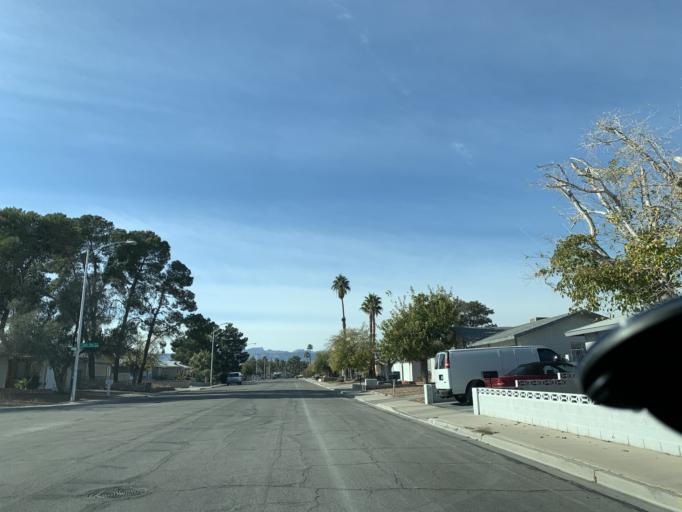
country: US
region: Nevada
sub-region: Clark County
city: Spring Valley
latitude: 36.1067
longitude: -115.2292
